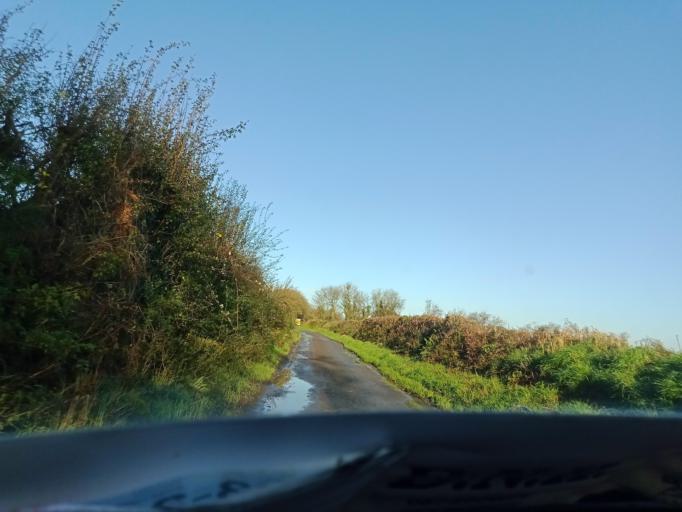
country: IE
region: Munster
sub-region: Waterford
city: Waterford
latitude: 52.2876
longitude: -7.1687
